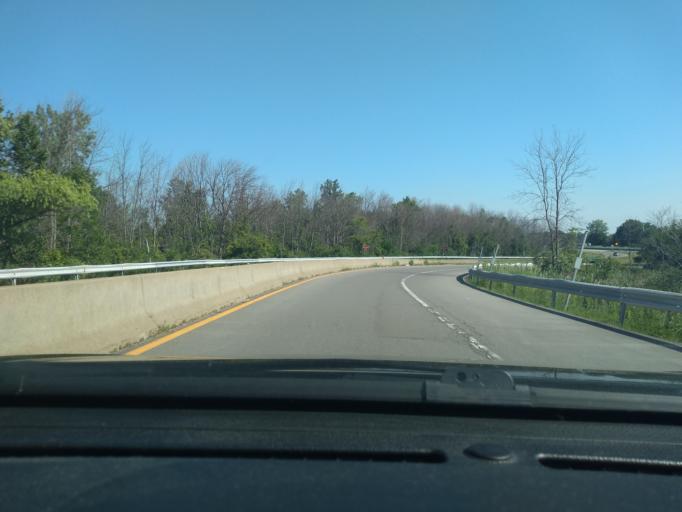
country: US
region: New York
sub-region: Erie County
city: West Seneca
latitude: 42.8295
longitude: -78.7933
